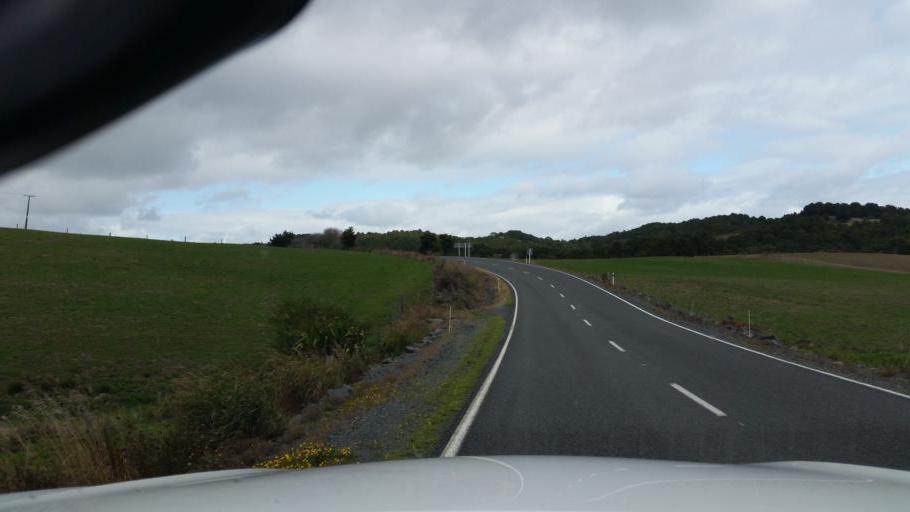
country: NZ
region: Northland
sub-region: Whangarei
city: Ruakaka
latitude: -36.0216
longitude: 174.2807
